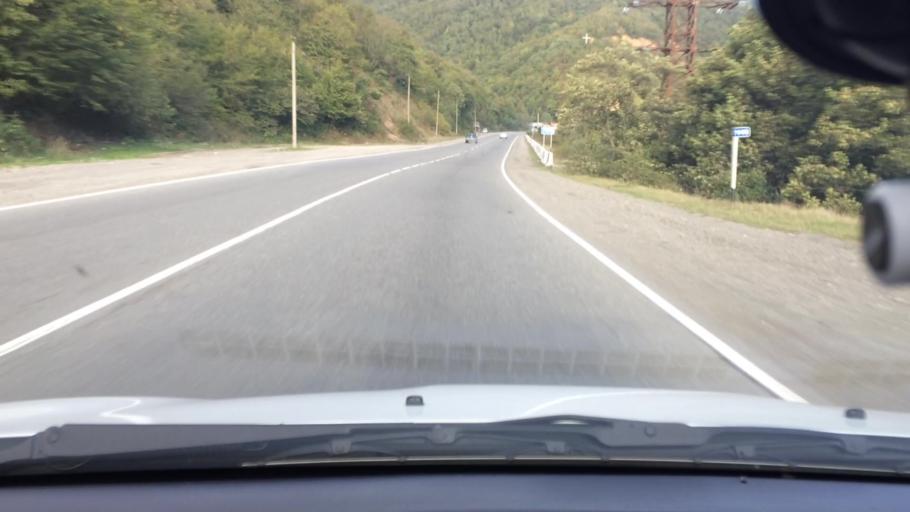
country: GE
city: Surami
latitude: 42.0407
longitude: 43.5056
